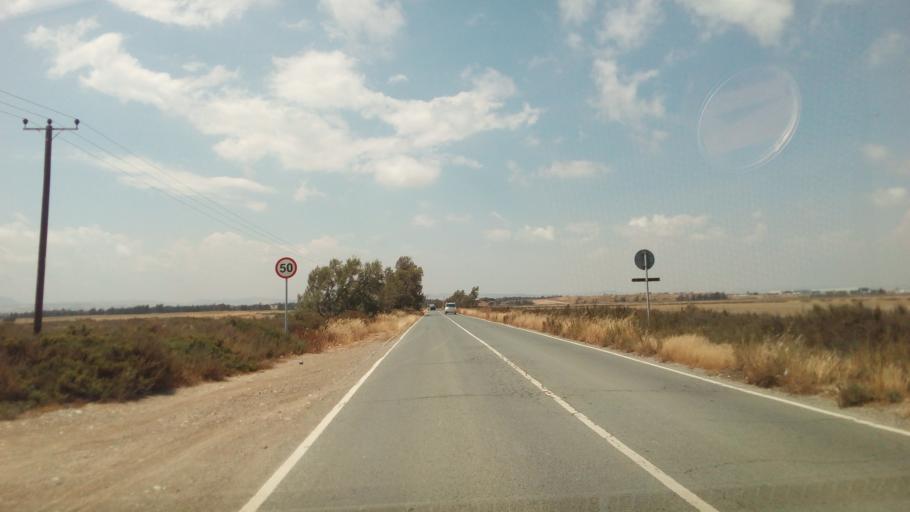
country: CY
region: Larnaka
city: Meneou
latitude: 34.8466
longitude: 33.6151
